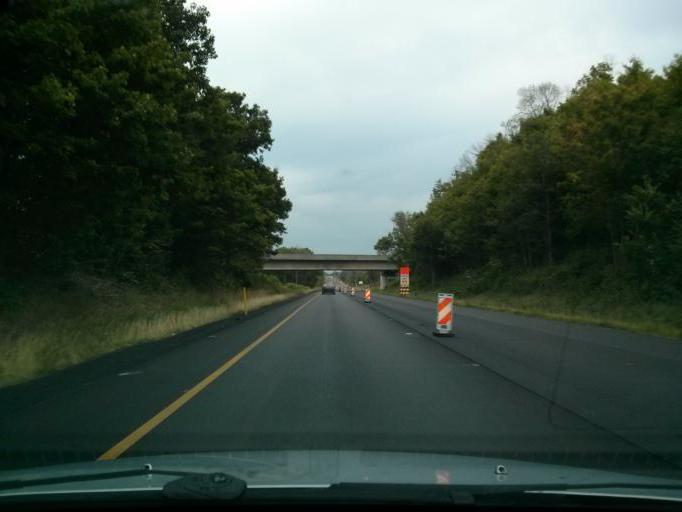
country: US
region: Pennsylvania
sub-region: Jefferson County
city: Reynoldsville
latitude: 41.1518
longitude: -78.8954
